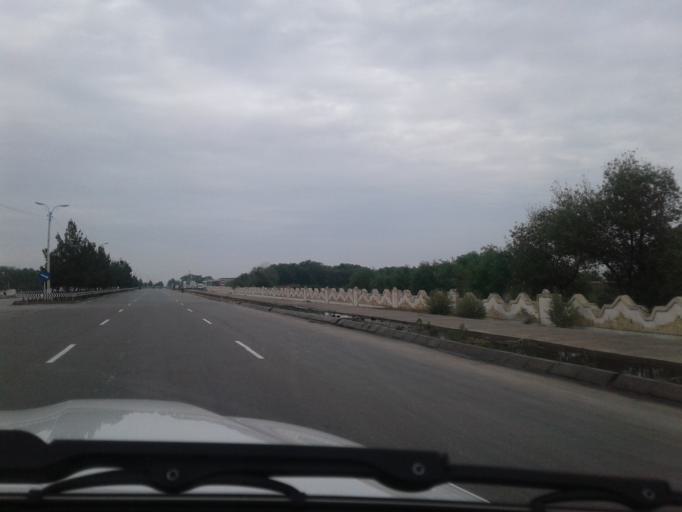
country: TM
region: Mary
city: Mary
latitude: 37.6091
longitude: 61.9310
